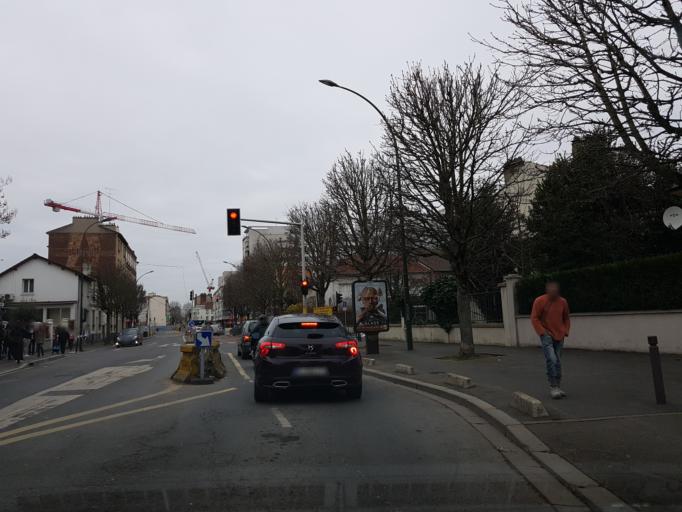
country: FR
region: Ile-de-France
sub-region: Departement du Val-de-Marne
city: Villejuif
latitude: 48.7886
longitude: 2.3701
